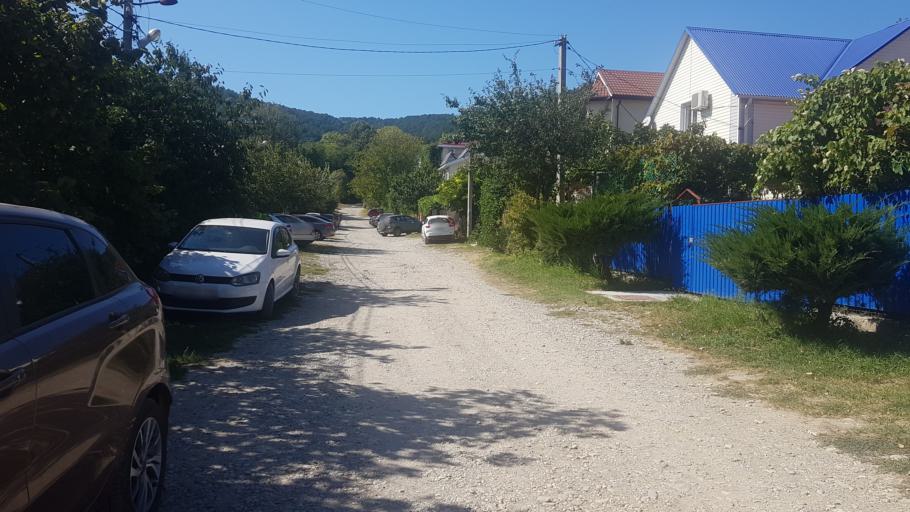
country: RU
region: Krasnodarskiy
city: Arkhipo-Osipovka
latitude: 44.3681
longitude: 38.5253
